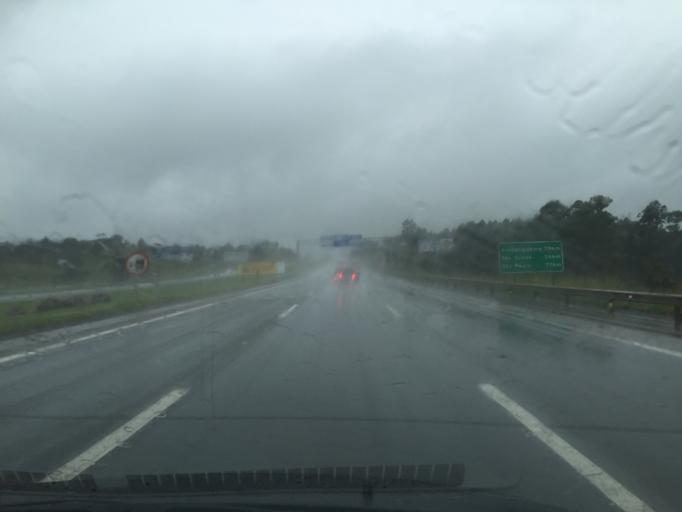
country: BR
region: Sao Paulo
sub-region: Itu
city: Itu
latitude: -23.4031
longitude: -47.3237
